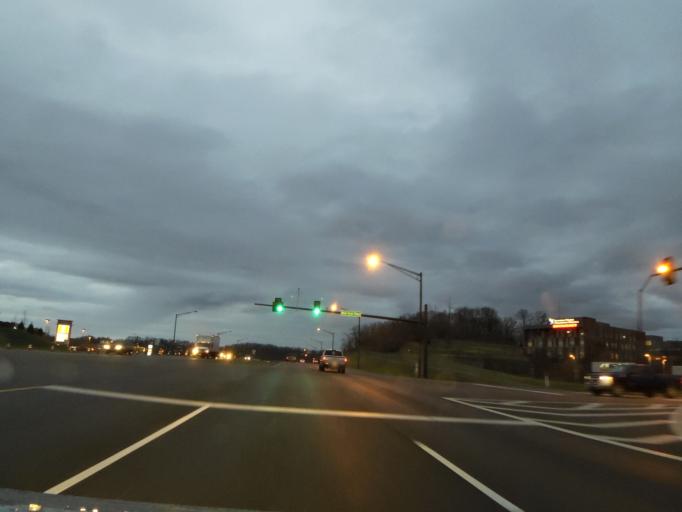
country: US
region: Tennessee
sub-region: Washington County
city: Midway
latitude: 36.3331
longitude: -82.4026
